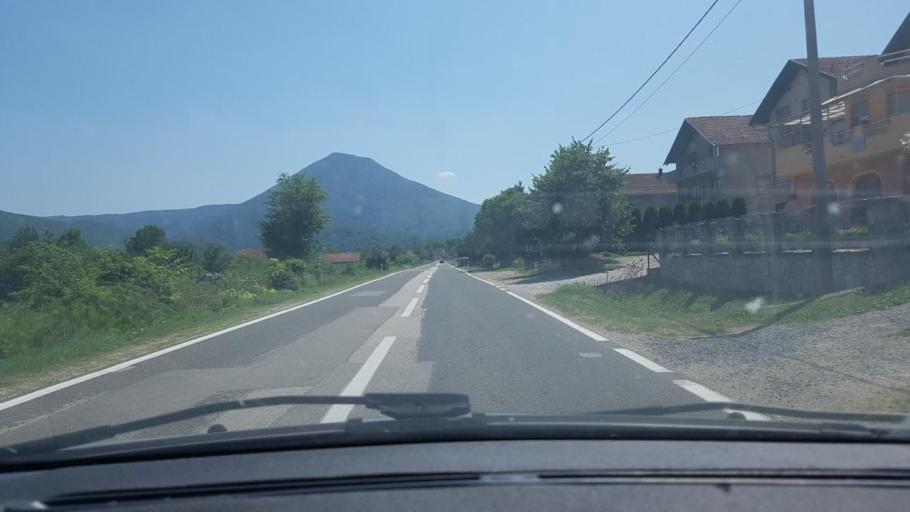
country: BA
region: Federation of Bosnia and Herzegovina
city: Bihac
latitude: 44.7682
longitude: 15.9444
